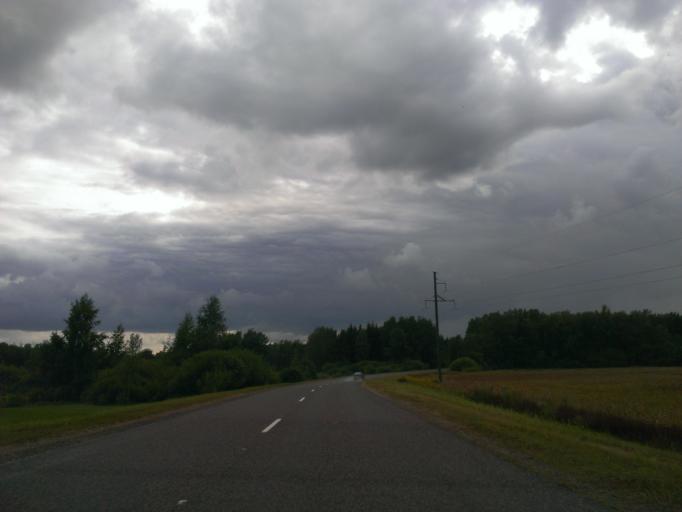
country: LV
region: Kegums
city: Kegums
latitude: 56.7686
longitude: 24.7676
